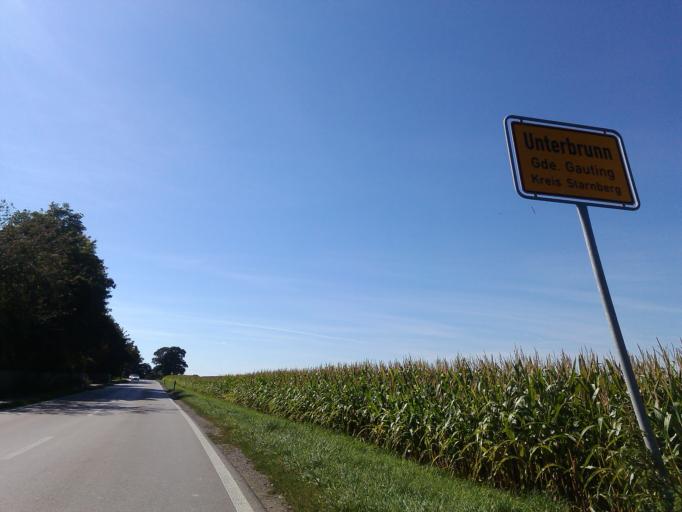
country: DE
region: Bavaria
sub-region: Upper Bavaria
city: Gauting
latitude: 48.0700
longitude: 11.3330
